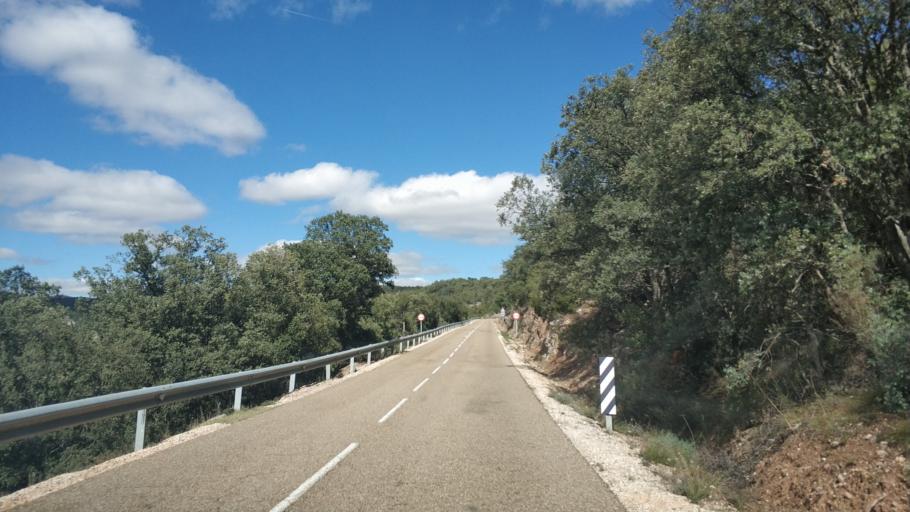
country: ES
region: Castille and Leon
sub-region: Provincia de Burgos
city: Retuerta
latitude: 42.0410
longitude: -3.4771
